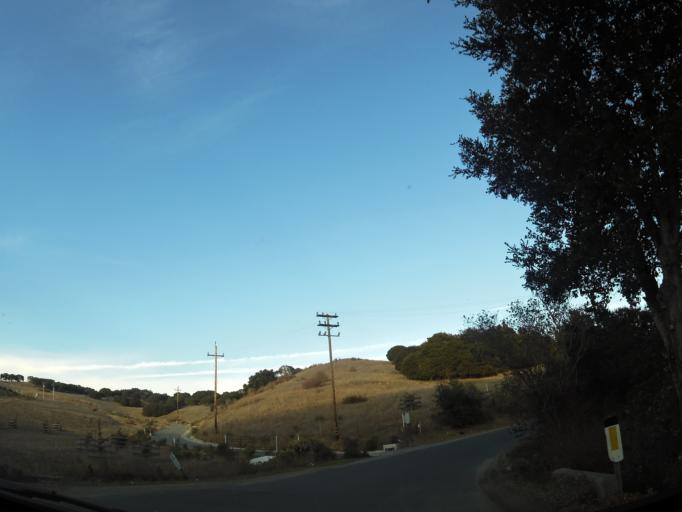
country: US
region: California
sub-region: Monterey County
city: Prunedale
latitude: 36.7778
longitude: -121.5980
